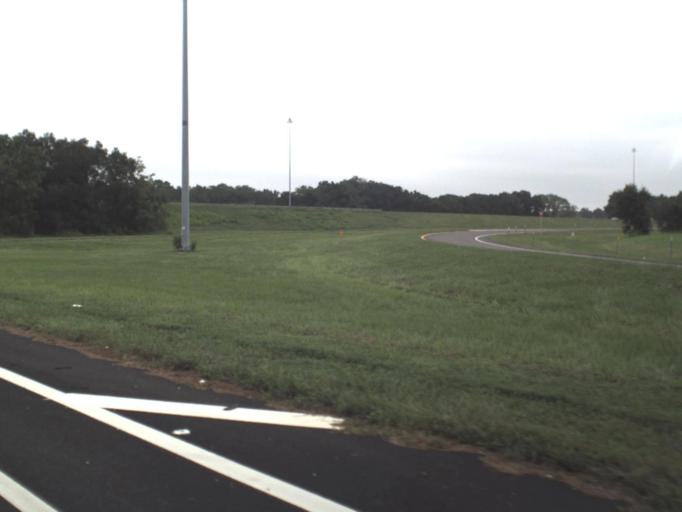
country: US
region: Florida
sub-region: Manatee County
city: Memphis
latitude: 27.5834
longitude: -82.5401
